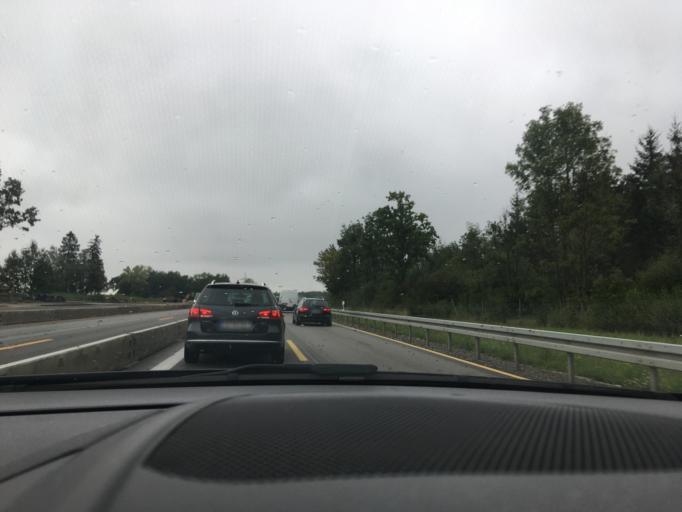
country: DE
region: Bavaria
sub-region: Upper Bavaria
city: Germering
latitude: 48.1059
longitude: 11.3417
